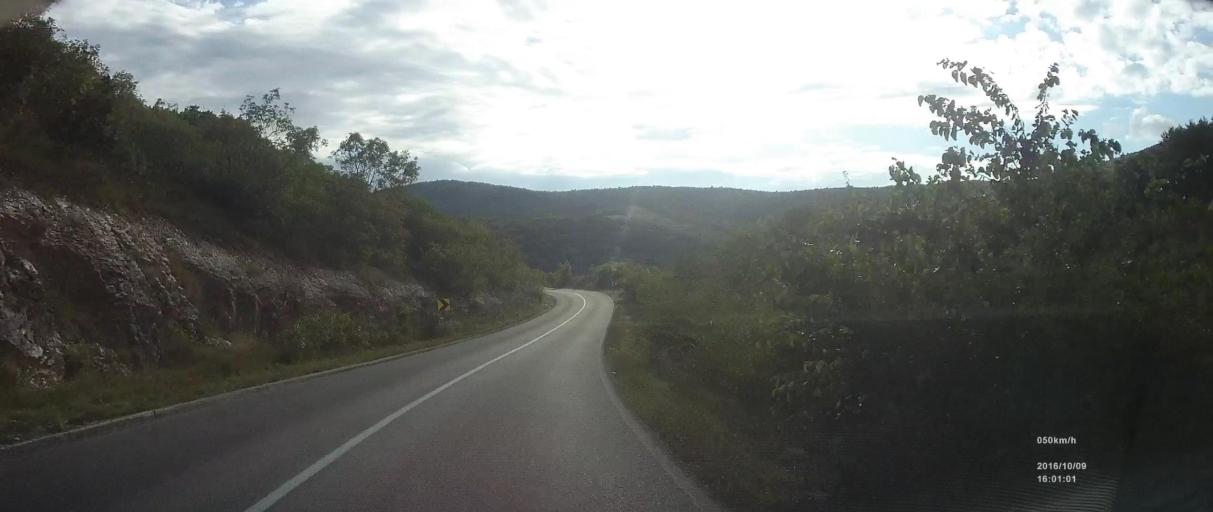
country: HR
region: Splitsko-Dalmatinska
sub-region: Grad Trogir
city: Trogir
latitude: 43.5672
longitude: 16.2464
